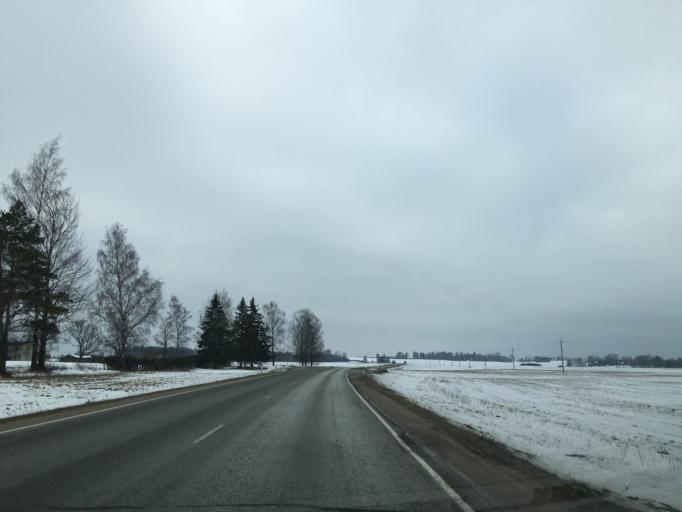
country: EE
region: Tartu
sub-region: Elva linn
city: Elva
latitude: 58.1256
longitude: 26.2439
